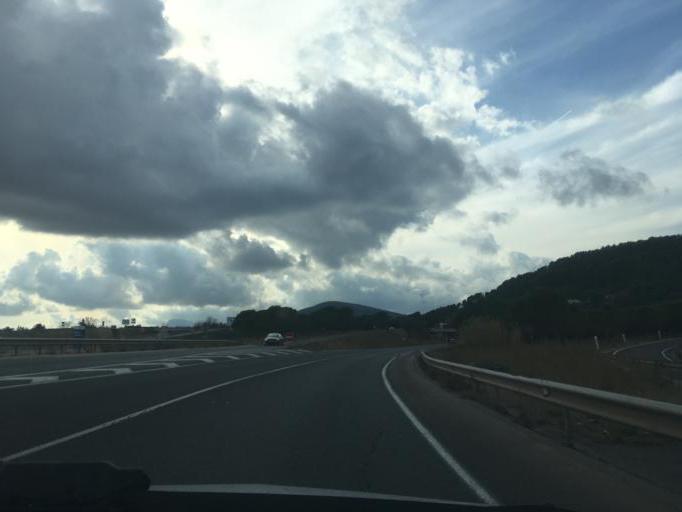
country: FR
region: Provence-Alpes-Cote d'Azur
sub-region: Departement du Var
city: Cuers
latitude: 43.2506
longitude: 6.0971
